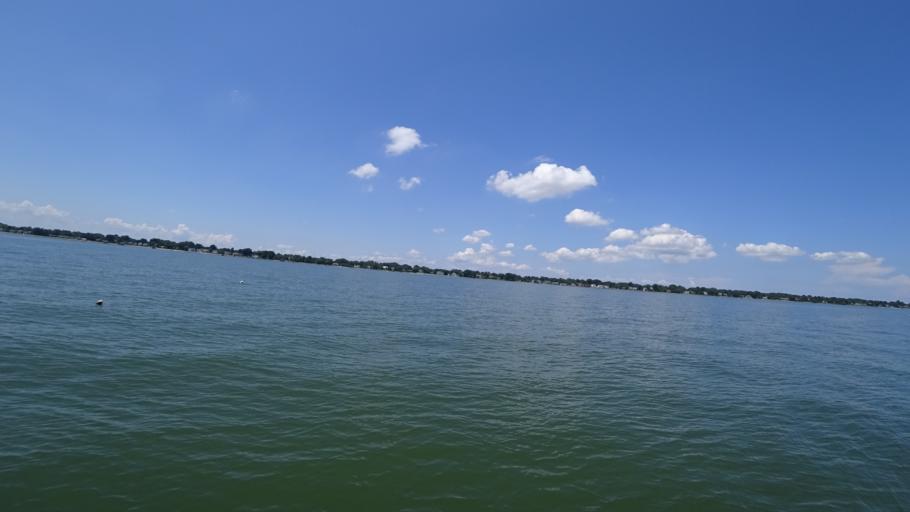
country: US
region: Virginia
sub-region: City of Hampton
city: Hampton
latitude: 36.9889
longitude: -76.3709
